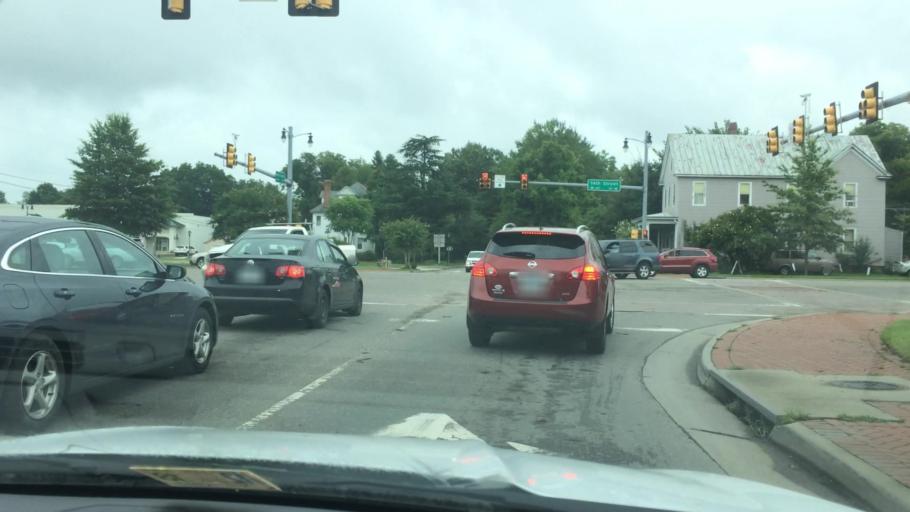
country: US
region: Virginia
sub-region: King William County
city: West Point
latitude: 37.5372
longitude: -76.7995
